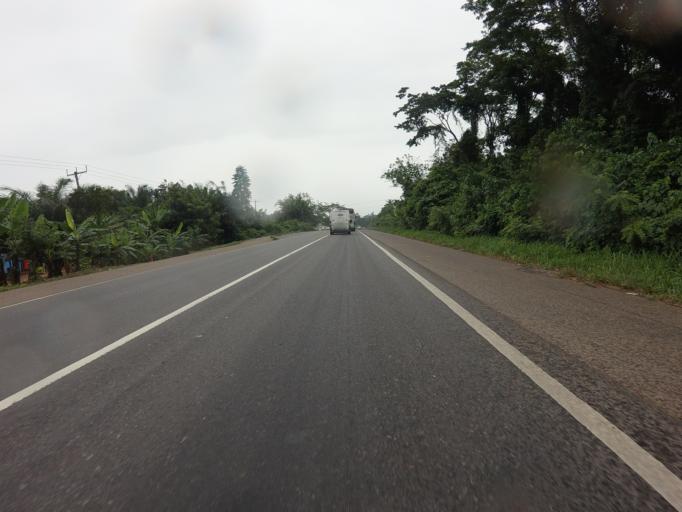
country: GH
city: Kibi
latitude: 6.1347
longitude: -0.4945
